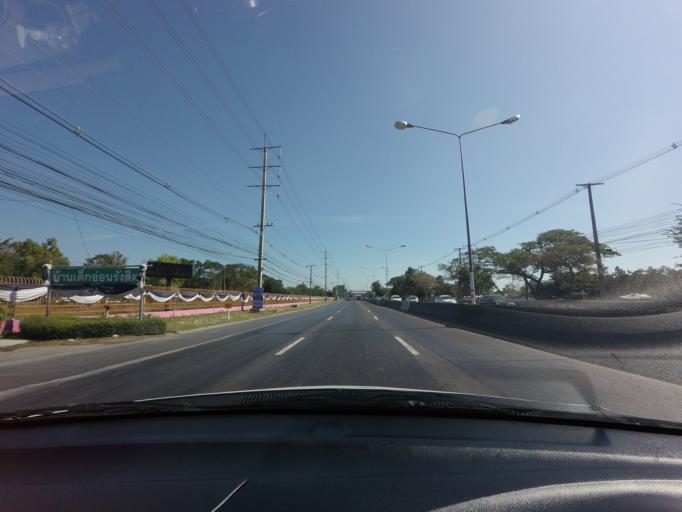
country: TH
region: Pathum Thani
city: Thanyaburi
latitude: 14.0113
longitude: 100.7134
